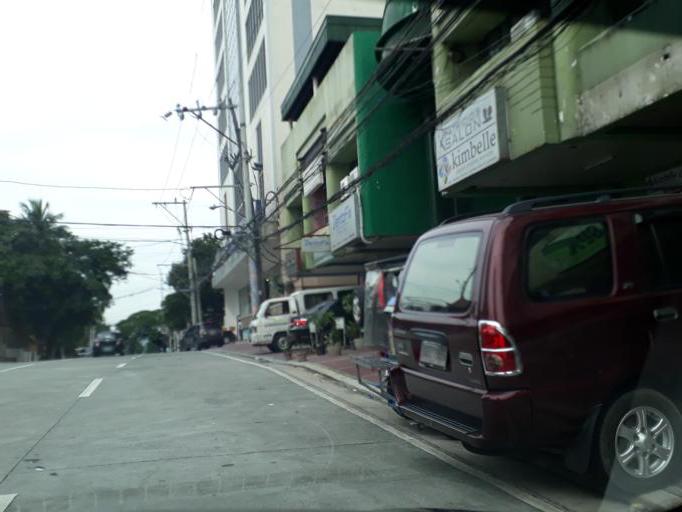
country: PH
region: Calabarzon
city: Del Monte
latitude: 14.6357
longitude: 121.0283
